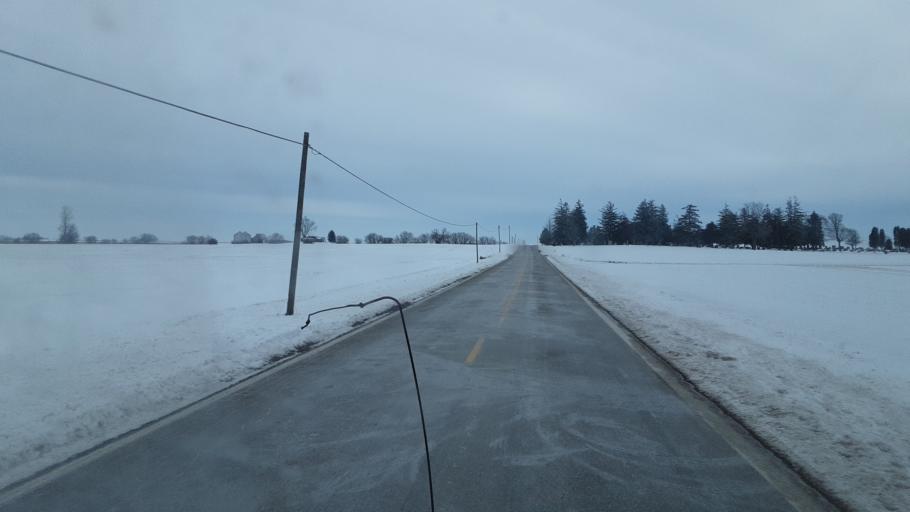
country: US
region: Ohio
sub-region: Madison County
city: Bethel
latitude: 39.7331
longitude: -83.4691
